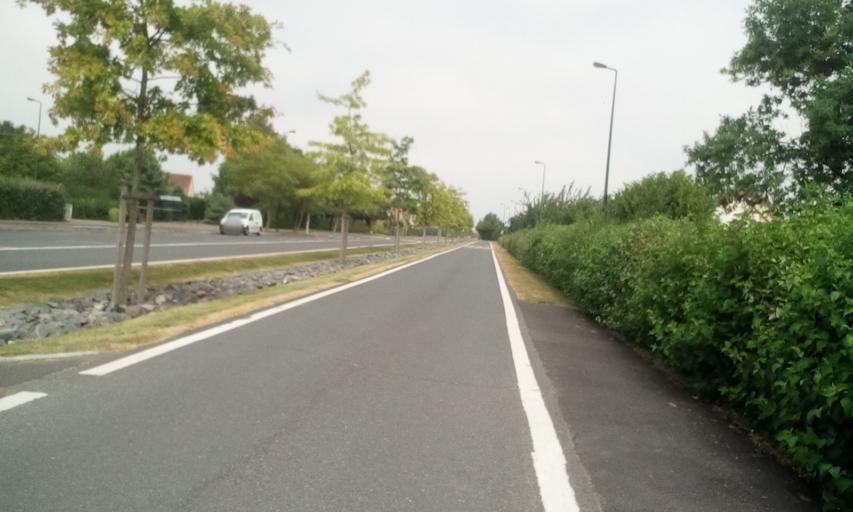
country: FR
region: Lower Normandy
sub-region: Departement du Calvados
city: Douvres-la-Delivrande
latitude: 49.2978
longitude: -0.3869
